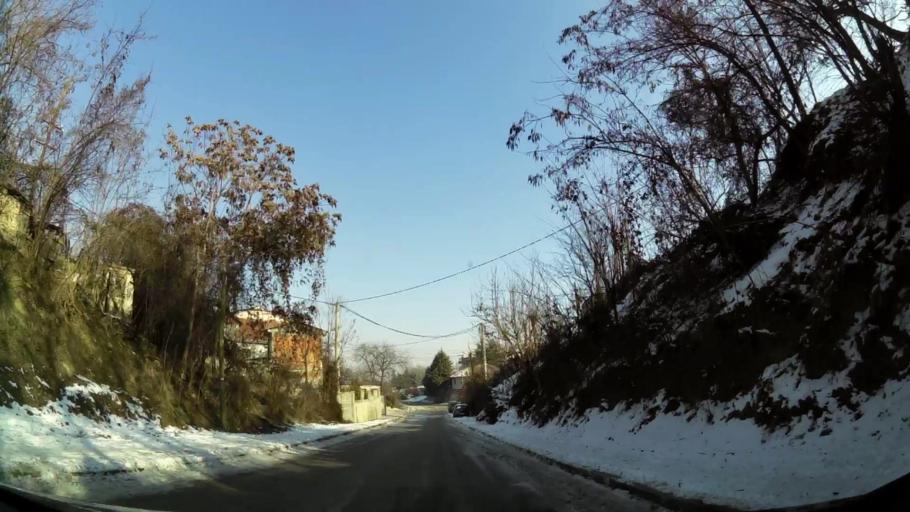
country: MK
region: Kisela Voda
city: Usje
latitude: 41.9664
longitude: 21.4471
